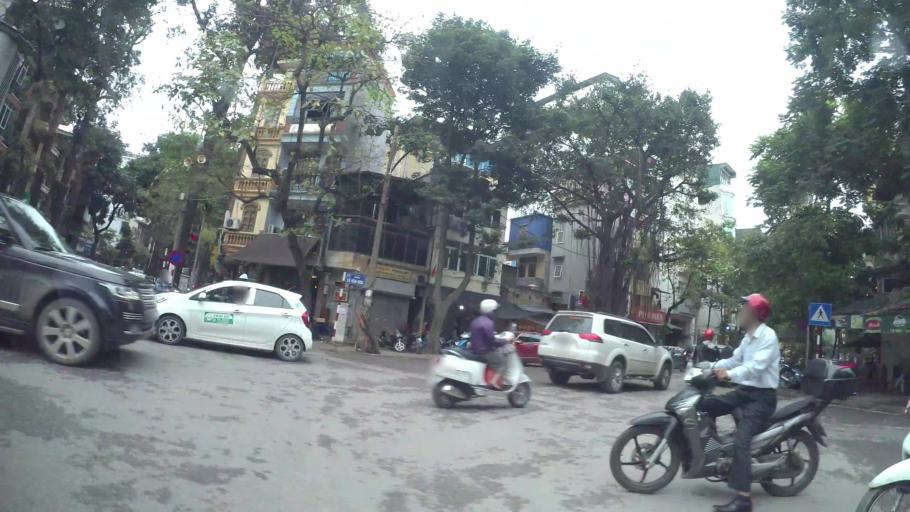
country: VN
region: Ha Noi
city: Hai BaTrung
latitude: 21.0184
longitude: 105.8548
